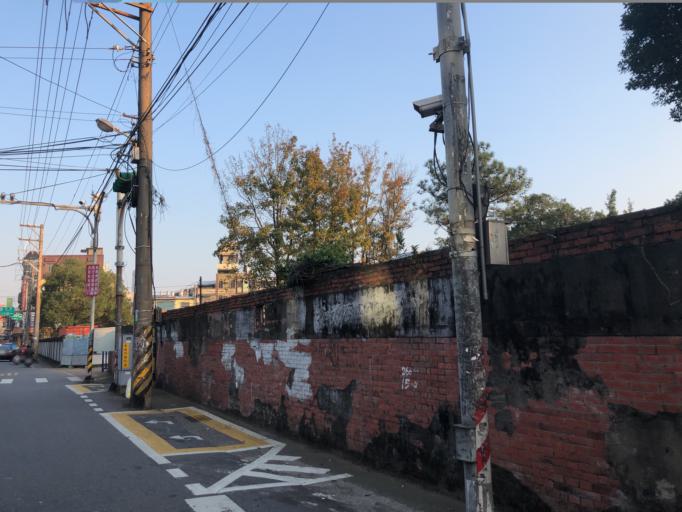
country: TW
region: Taiwan
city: Taoyuan City
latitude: 24.9595
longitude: 121.2931
